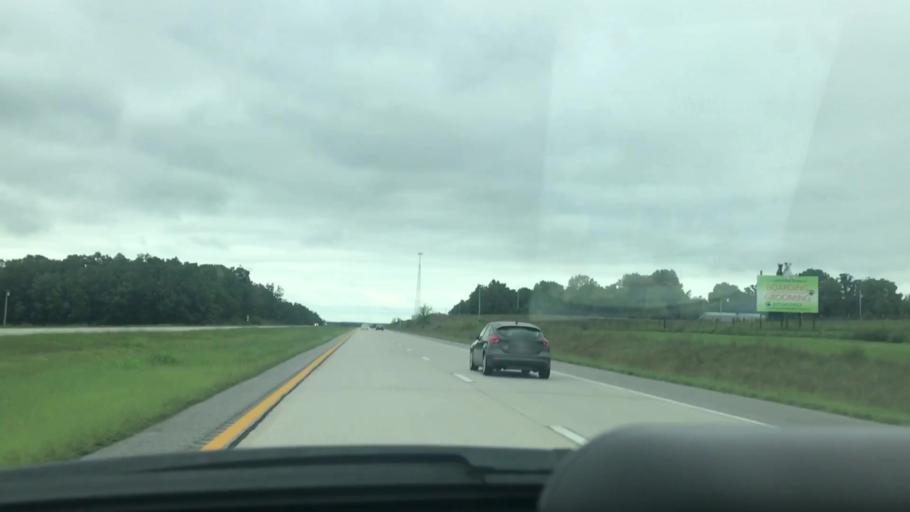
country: US
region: Missouri
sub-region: Greene County
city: Fair Grove
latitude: 37.5012
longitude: -93.1389
